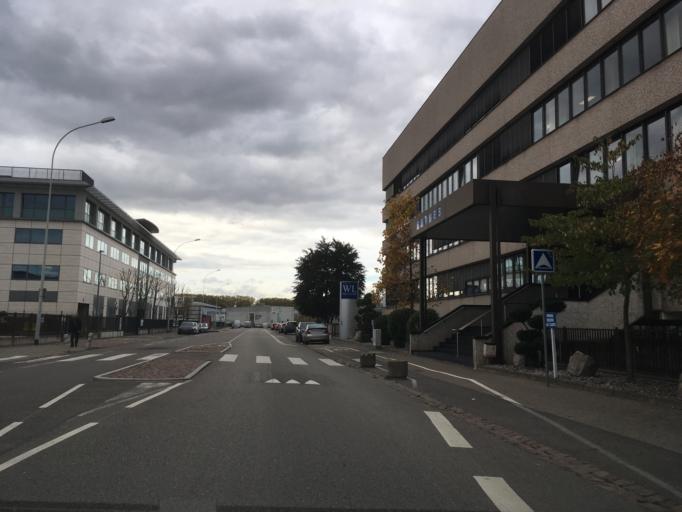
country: FR
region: Alsace
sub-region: Departement du Bas-Rhin
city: Strasbourg
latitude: 48.5539
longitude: 7.7415
